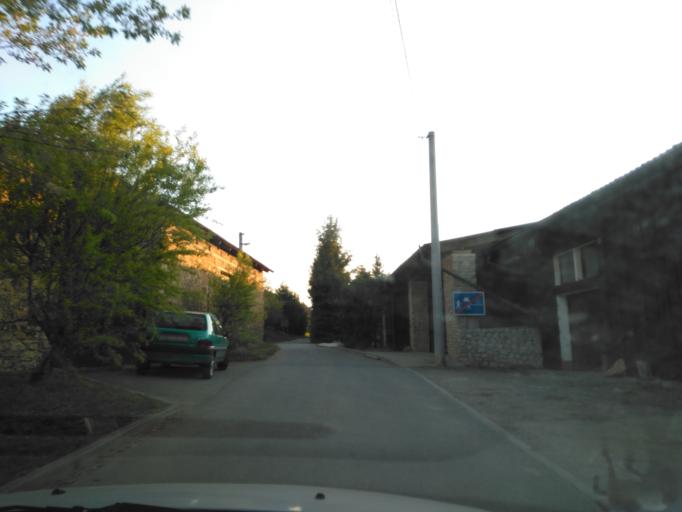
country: CZ
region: Central Bohemia
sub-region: Okres Beroun
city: Kraluv Dvur
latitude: 49.9029
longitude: 14.0344
